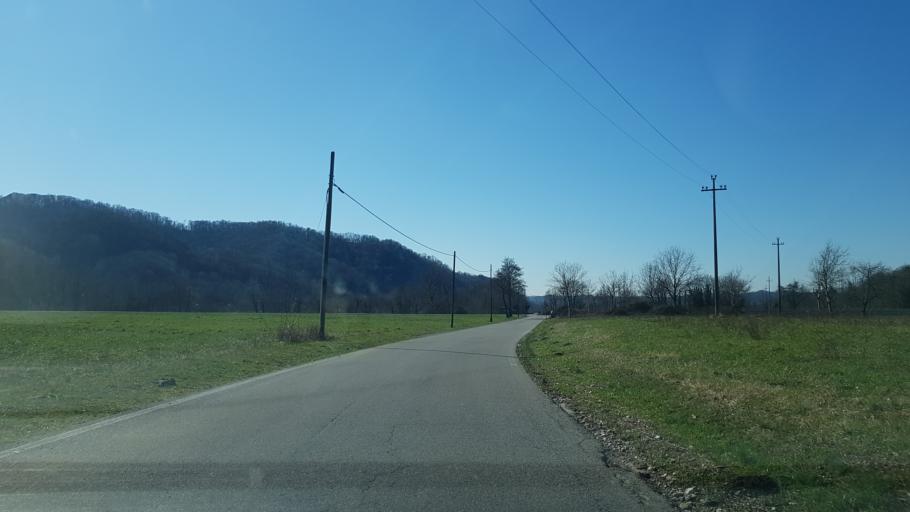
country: IT
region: Friuli Venezia Giulia
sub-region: Provincia di Udine
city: Nimis
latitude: 46.2050
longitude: 13.2905
